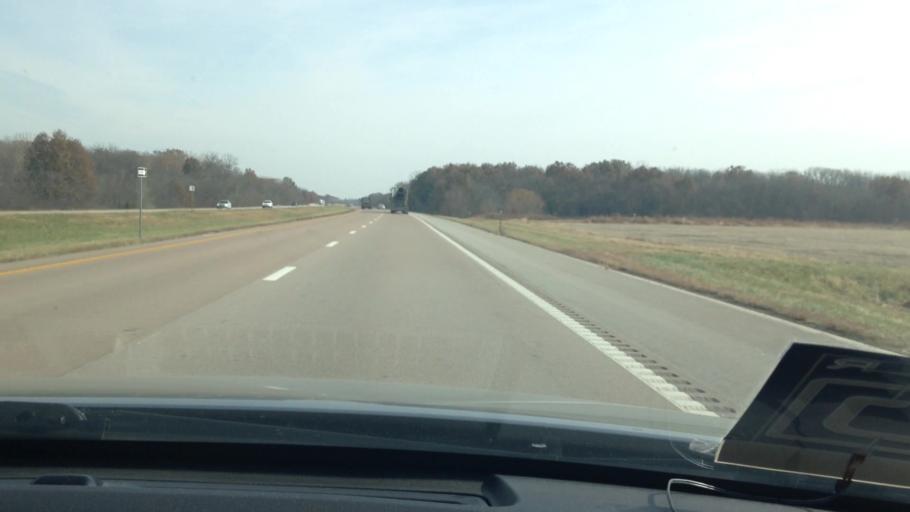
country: US
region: Missouri
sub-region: Henry County
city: Clinton
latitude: 38.4278
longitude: -93.9097
